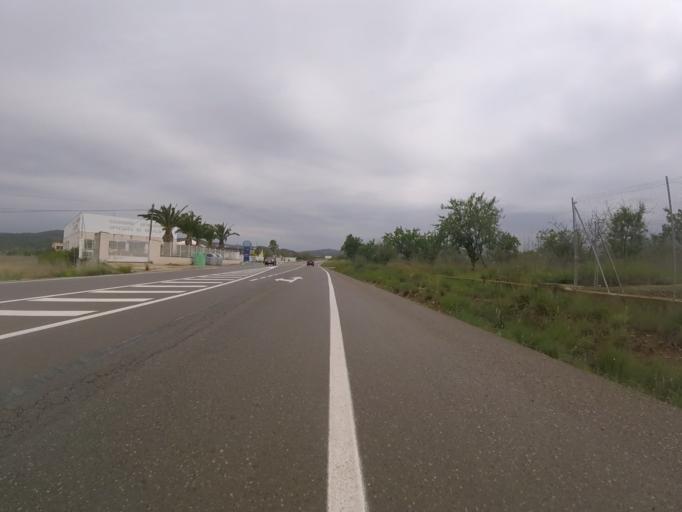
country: ES
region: Valencia
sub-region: Provincia de Castello
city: Alcoceber
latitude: 40.2554
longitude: 0.2454
